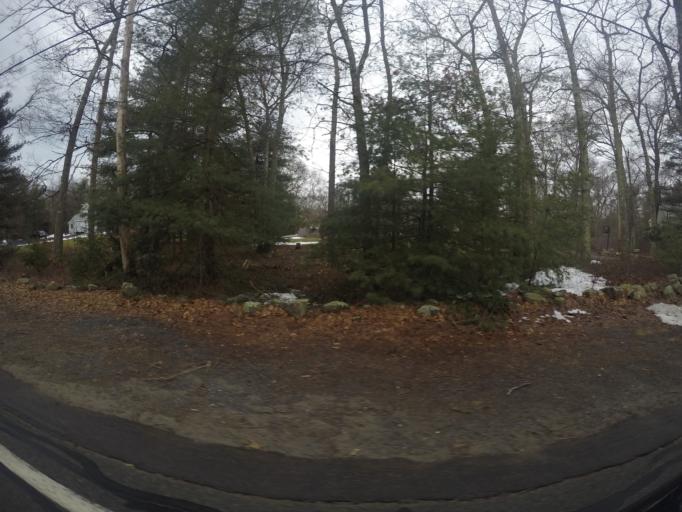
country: US
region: Massachusetts
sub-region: Bristol County
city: Easton
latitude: 42.0605
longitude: -71.1670
